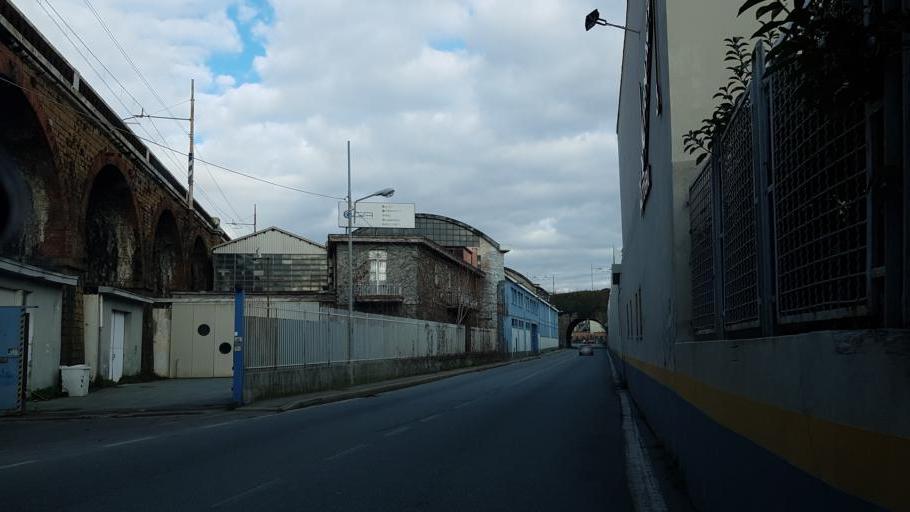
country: IT
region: Liguria
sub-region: Provincia di Genova
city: Genoa
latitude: 44.4383
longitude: 8.8878
